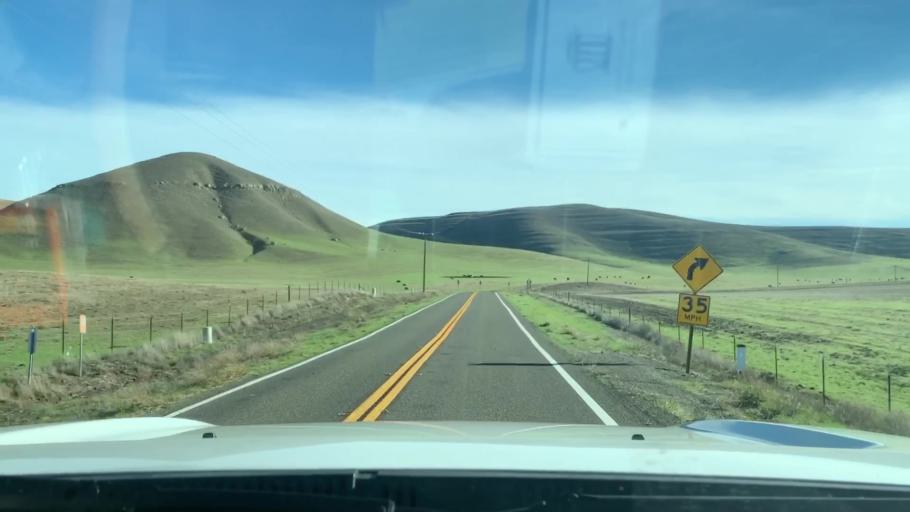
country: US
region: California
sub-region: Monterey County
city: King City
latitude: 36.1582
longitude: -120.9844
